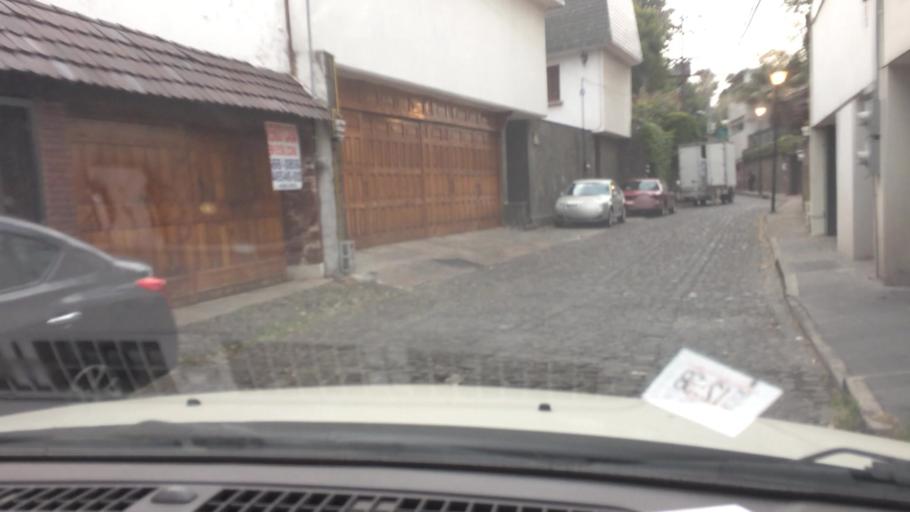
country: MX
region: Mexico City
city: Alvaro Obregon
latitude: 19.3527
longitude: -99.1943
